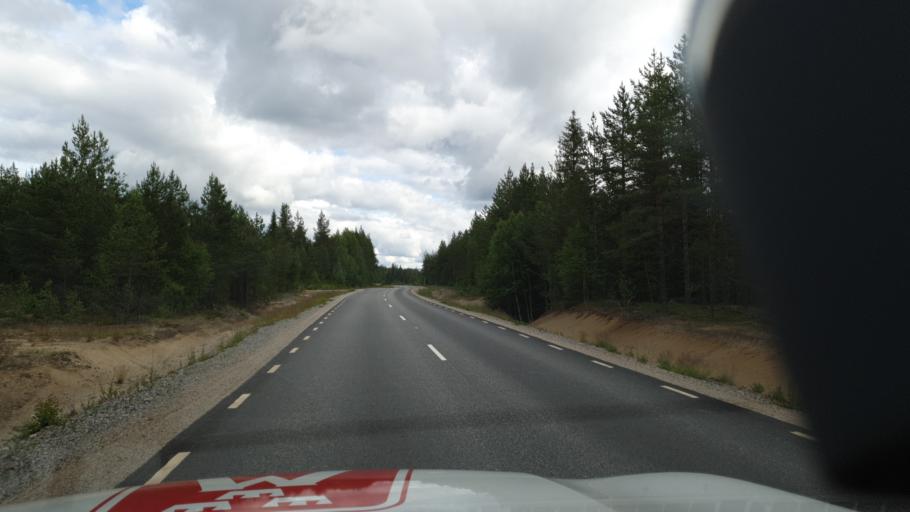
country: SE
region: Vaesterbotten
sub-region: Lycksele Kommun
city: Lycksele
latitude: 64.4681
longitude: 19.1613
